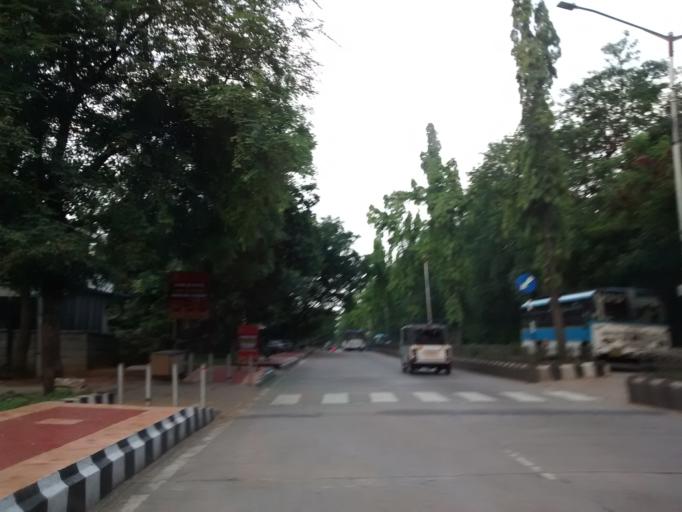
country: IN
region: Andhra Pradesh
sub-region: Chittoor
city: Akkarampalle
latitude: 13.6521
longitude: 79.4176
